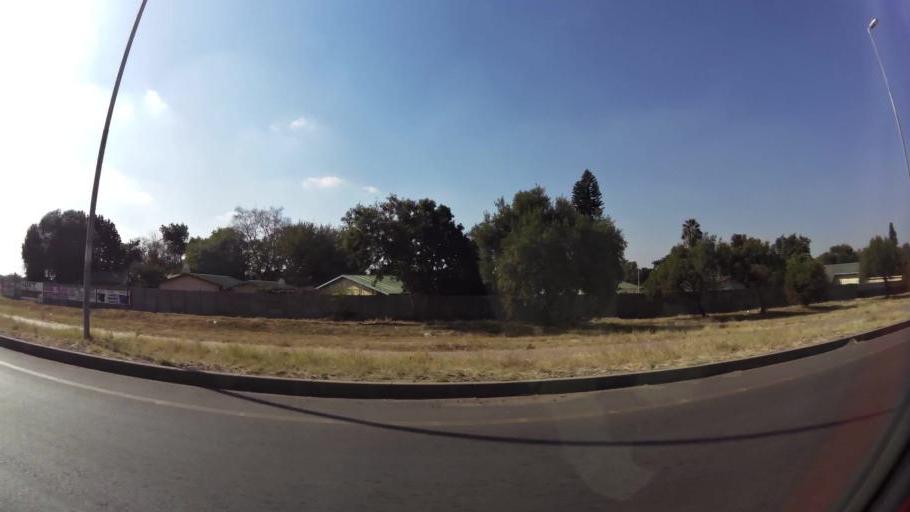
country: ZA
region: North-West
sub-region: Bojanala Platinum District Municipality
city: Rustenburg
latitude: -25.6547
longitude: 27.2210
